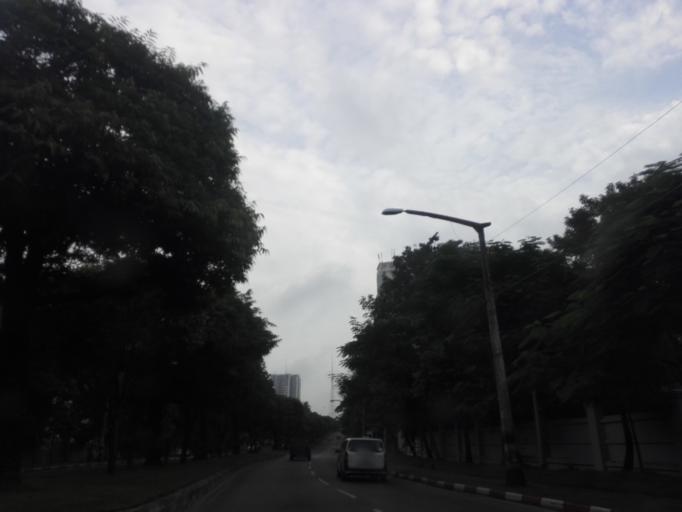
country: MM
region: Yangon
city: Yangon
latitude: 16.8059
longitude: 96.1417
